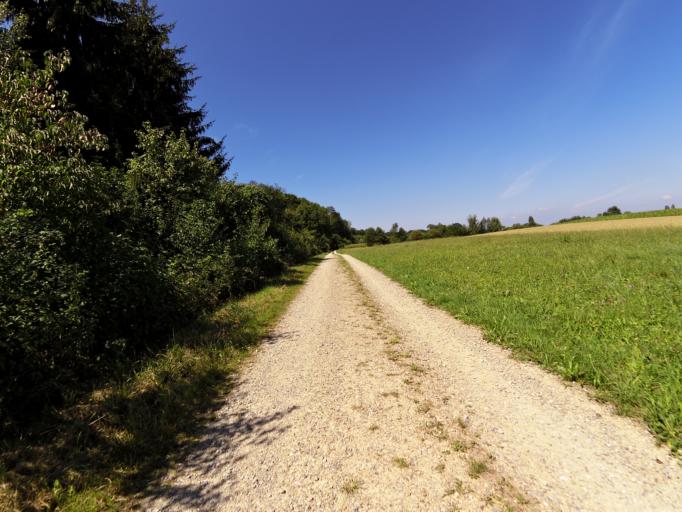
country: CH
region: Thurgau
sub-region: Kreuzlingen District
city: Tagerwilen
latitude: 47.6390
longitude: 9.1465
